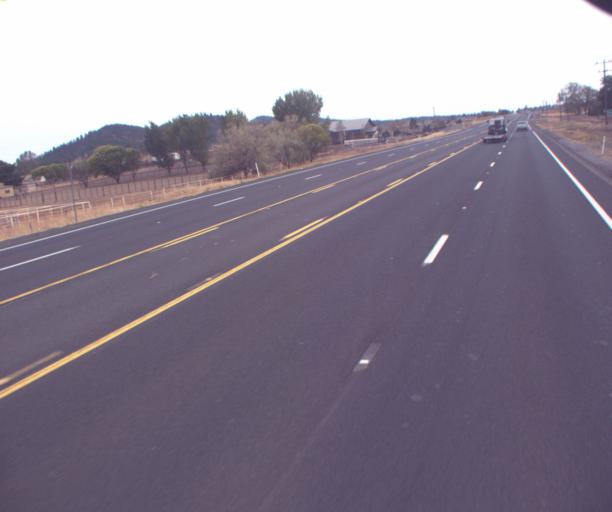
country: US
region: Arizona
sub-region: Coconino County
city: Flagstaff
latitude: 35.3097
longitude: -111.5427
